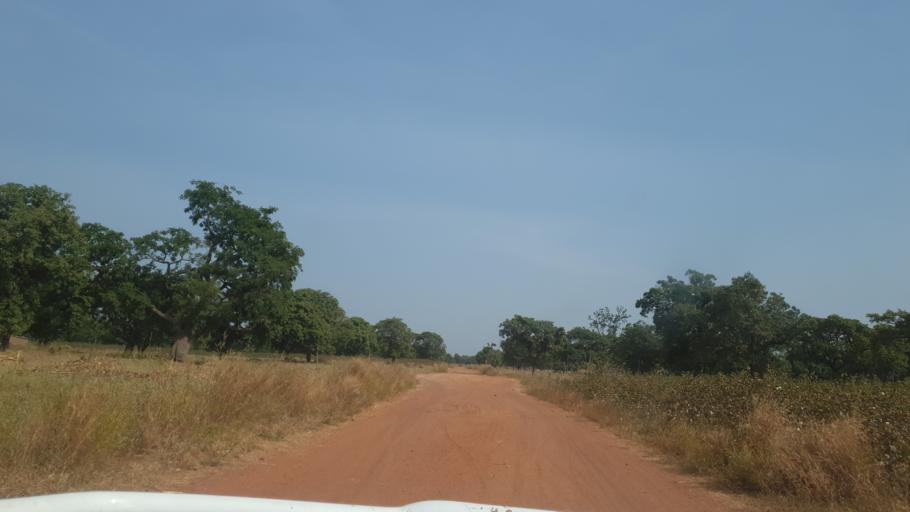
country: ML
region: Koulikoro
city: Dioila
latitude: 12.2293
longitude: -6.2221
